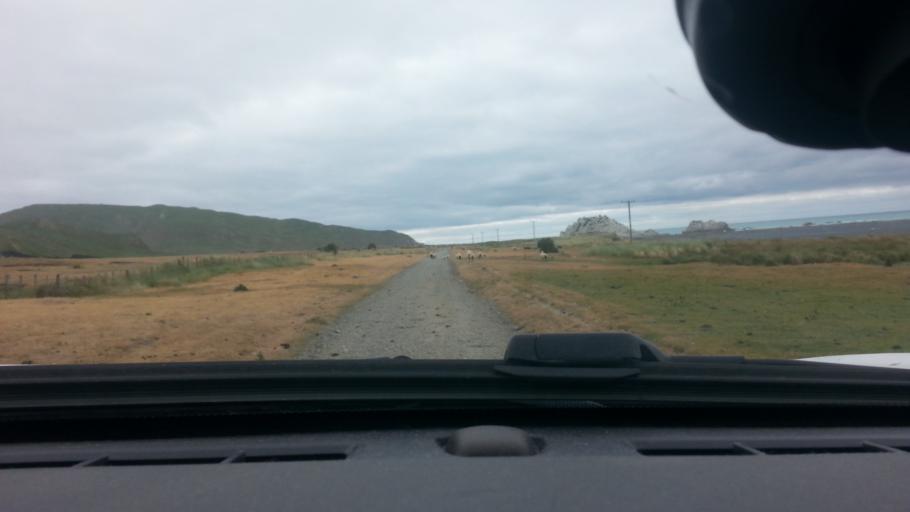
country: NZ
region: Wellington
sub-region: South Wairarapa District
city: Waipawa
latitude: -41.5666
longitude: 175.3888
